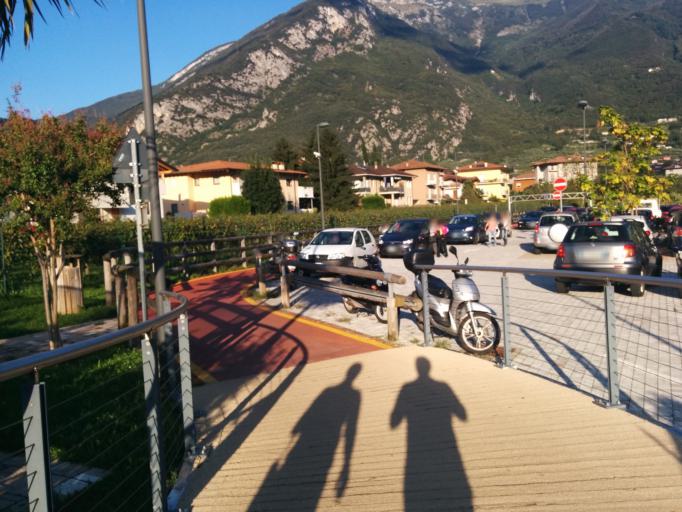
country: IT
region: Trentino-Alto Adige
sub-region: Provincia di Trento
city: Arco
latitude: 45.9164
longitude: 10.8896
